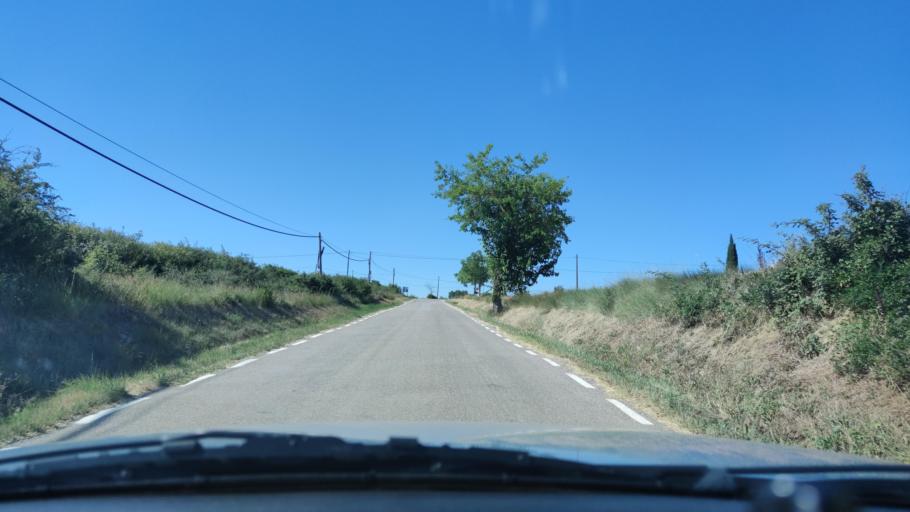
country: ES
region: Catalonia
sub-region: Provincia de Lleida
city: Solsona
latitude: 41.9785
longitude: 1.5037
